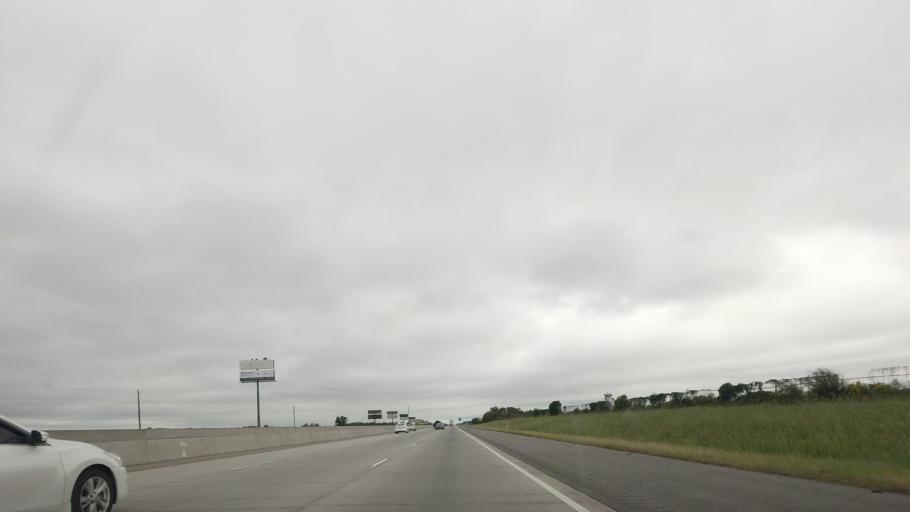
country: US
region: Georgia
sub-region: Tift County
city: Unionville
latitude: 31.3842
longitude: -83.4965
